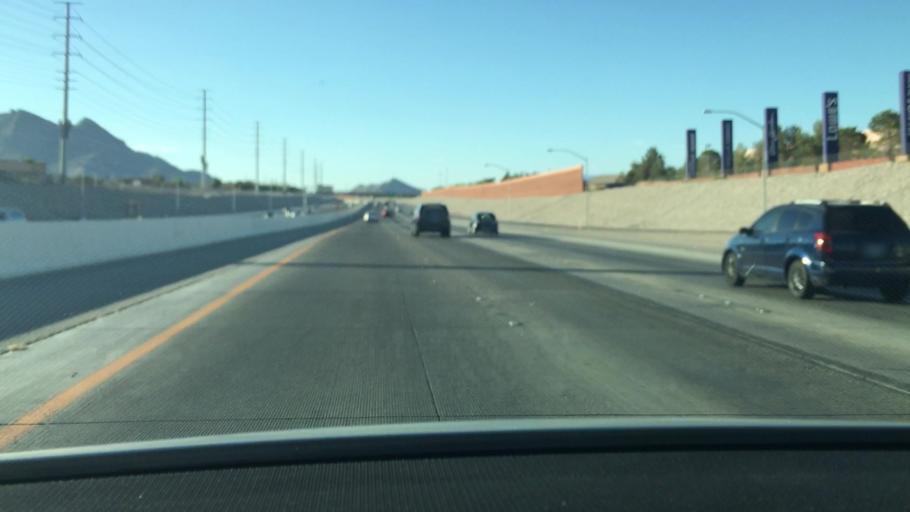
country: US
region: Nevada
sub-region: Clark County
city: Summerlin South
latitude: 36.1622
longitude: -115.3373
